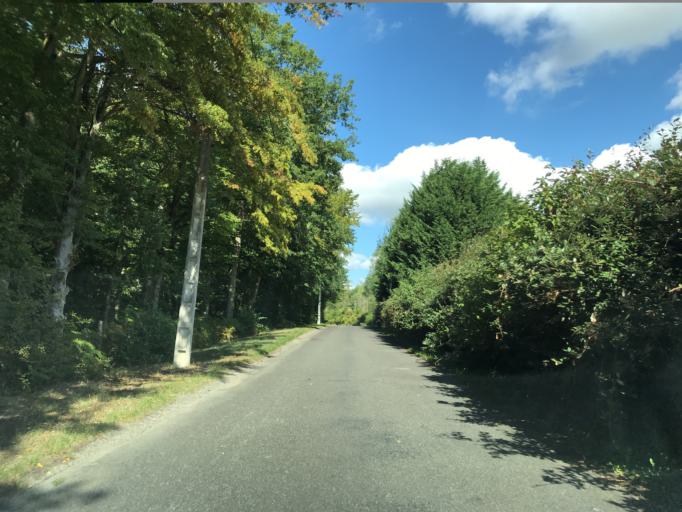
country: FR
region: Haute-Normandie
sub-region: Departement de l'Eure
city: La Chapelle-Reanville
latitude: 49.0886
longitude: 1.3963
